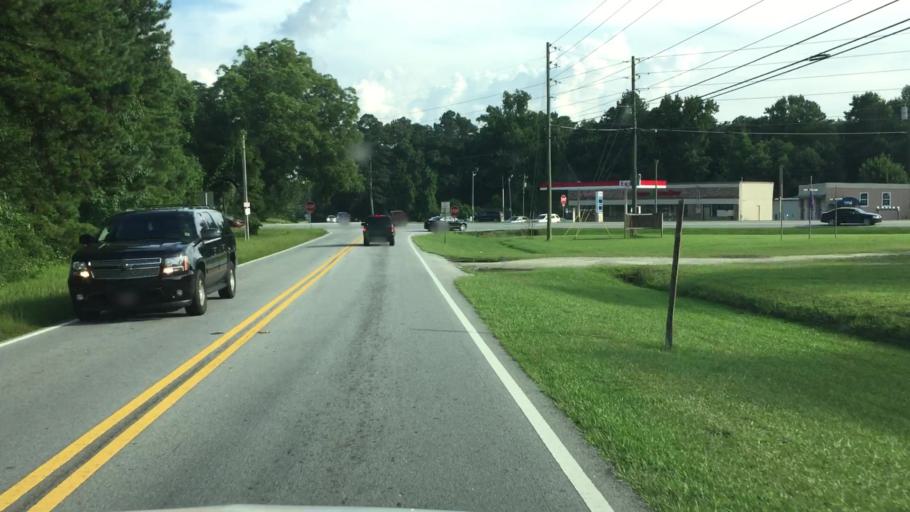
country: US
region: Georgia
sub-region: DeKalb County
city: Pine Mountain
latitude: 33.6080
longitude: -84.1371
